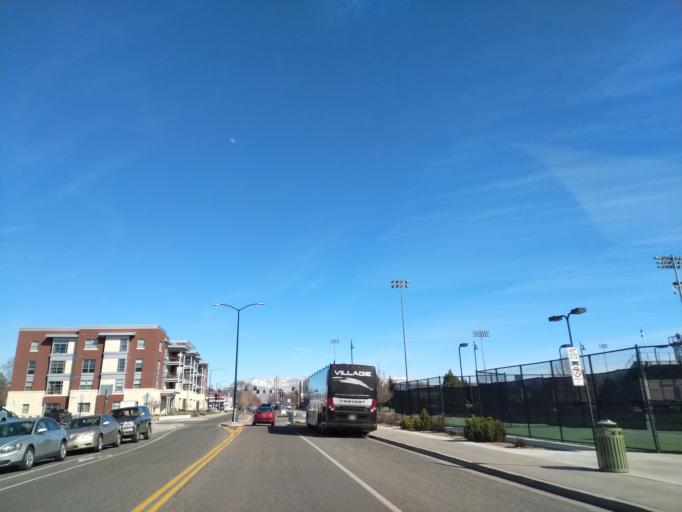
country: US
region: Colorado
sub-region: Mesa County
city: Grand Junction
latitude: 39.0846
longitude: -108.5546
